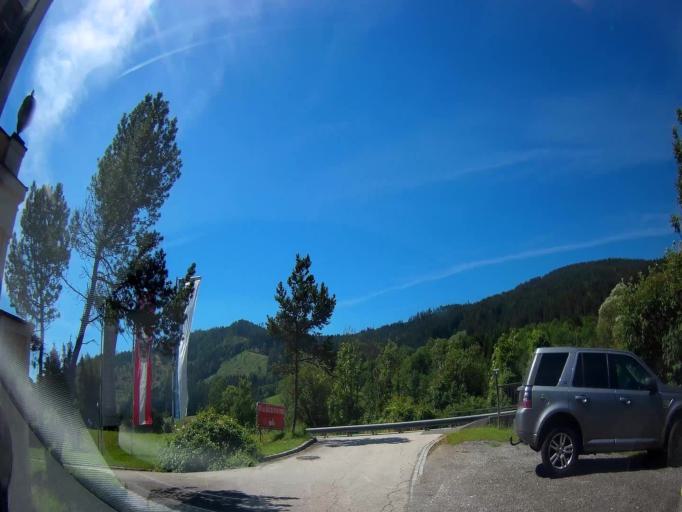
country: AT
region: Carinthia
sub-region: Politischer Bezirk Sankt Veit an der Glan
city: Micheldorf
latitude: 46.8909
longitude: 14.4396
